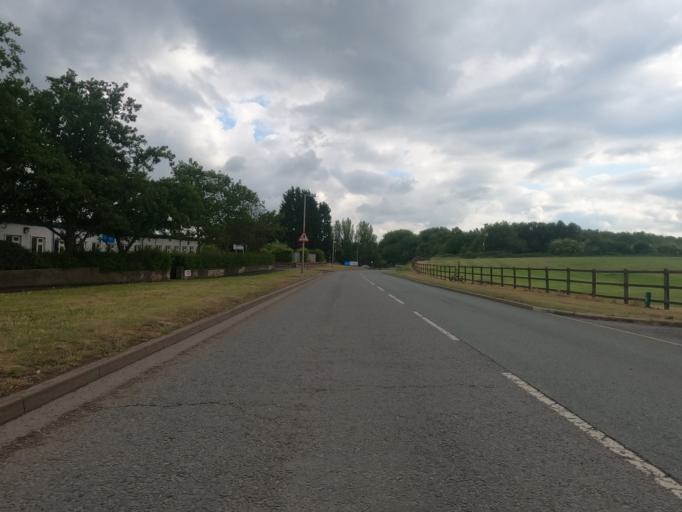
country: GB
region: England
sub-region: Cheshire West and Chester
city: Winsford
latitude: 53.2077
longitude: -2.5212
